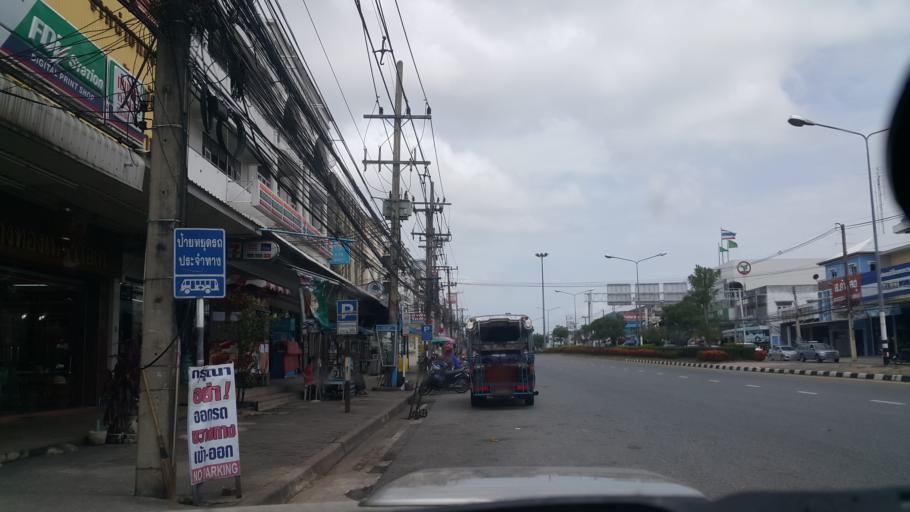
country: TH
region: Rayong
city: Ban Chang
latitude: 12.7241
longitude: 101.0542
